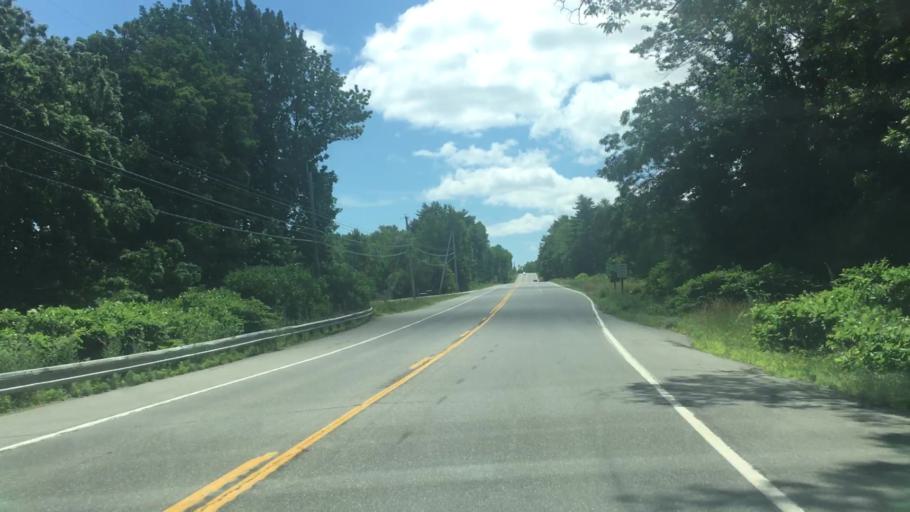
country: US
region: Maine
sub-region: Waldo County
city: Northport
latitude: 44.3685
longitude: -68.9810
